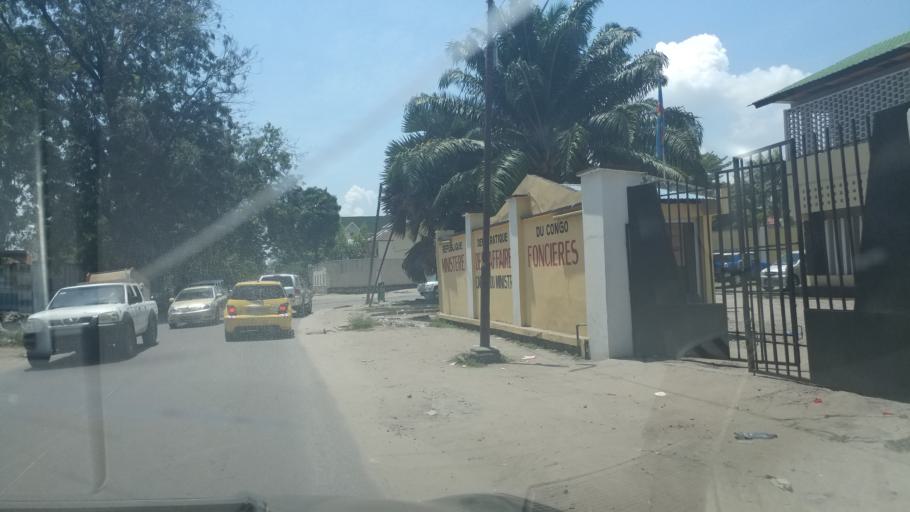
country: CD
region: Kinshasa
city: Kinshasa
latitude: -4.3191
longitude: 15.2805
